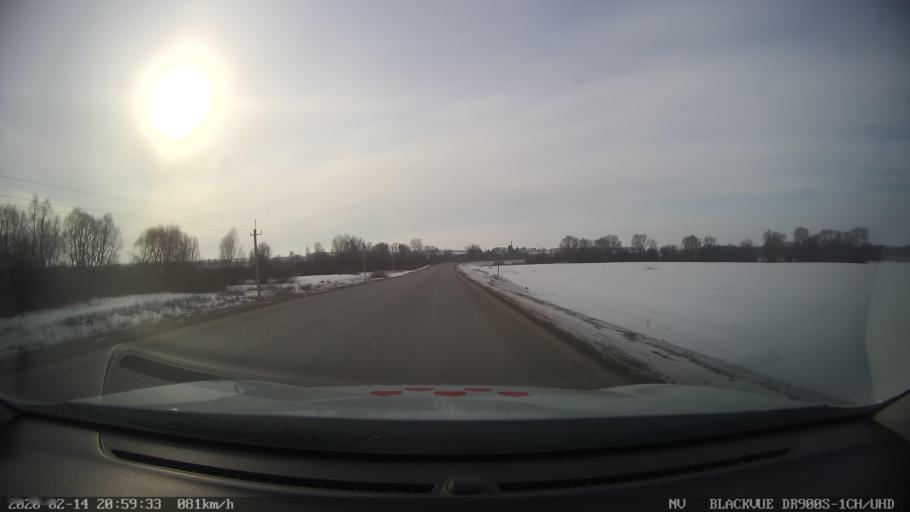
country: RU
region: Tatarstan
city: Kuybyshevskiy Zaton
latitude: 55.1776
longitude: 49.2367
